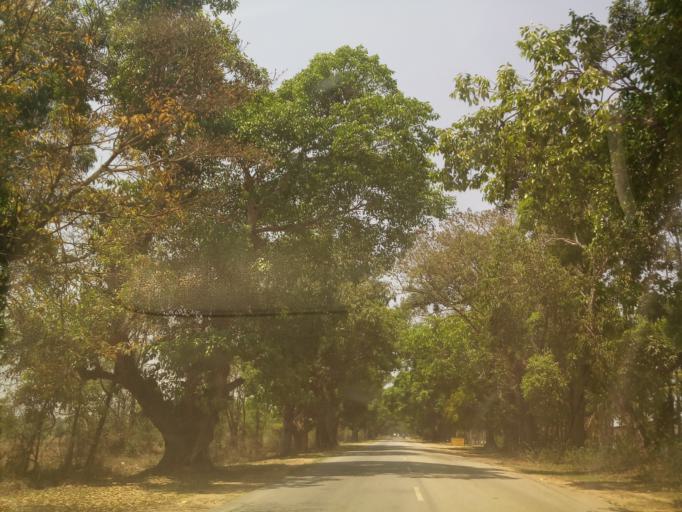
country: IN
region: Karnataka
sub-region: Hassan
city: Alur
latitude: 12.9476
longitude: 75.9547
